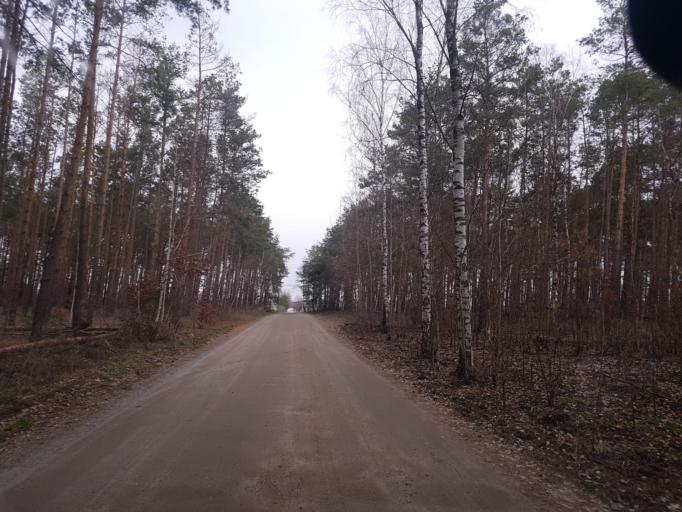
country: DE
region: Brandenburg
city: Finsterwalde
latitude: 51.6564
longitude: 13.6768
